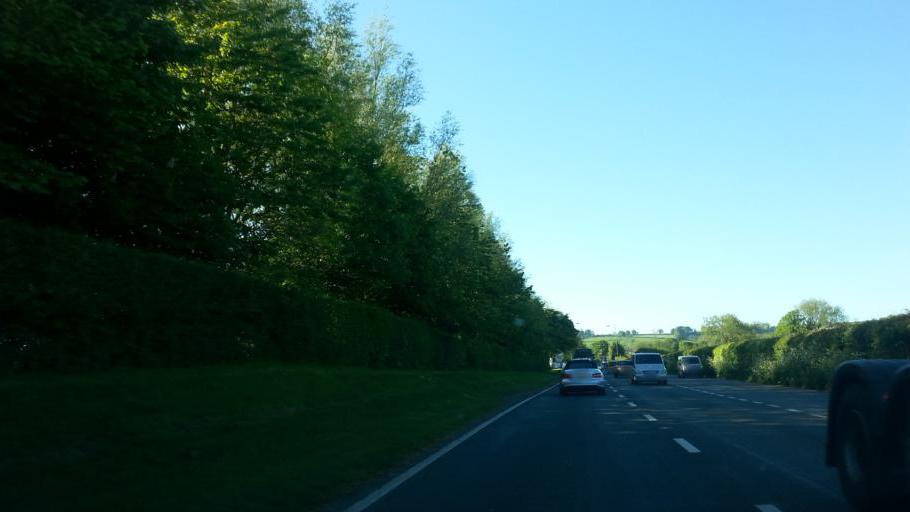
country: GB
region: England
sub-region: Somerset
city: Evercreech
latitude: 51.1541
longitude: -2.5222
